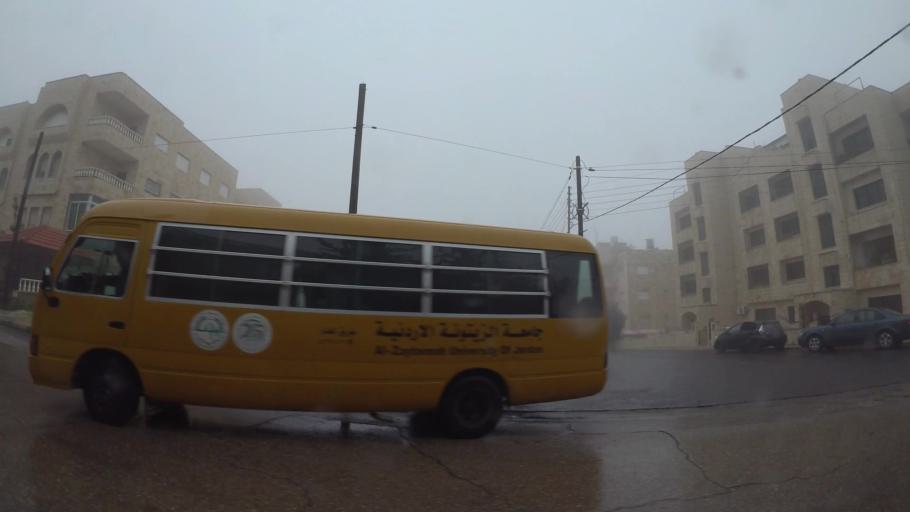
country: JO
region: Amman
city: Al Jubayhah
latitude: 32.0191
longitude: 35.8755
